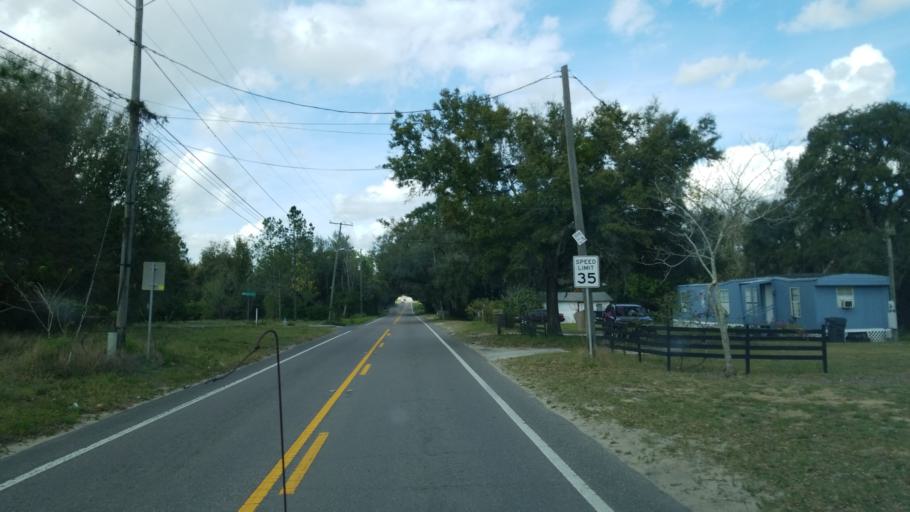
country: US
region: Florida
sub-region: Polk County
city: Haines City
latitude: 28.1098
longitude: -81.6068
